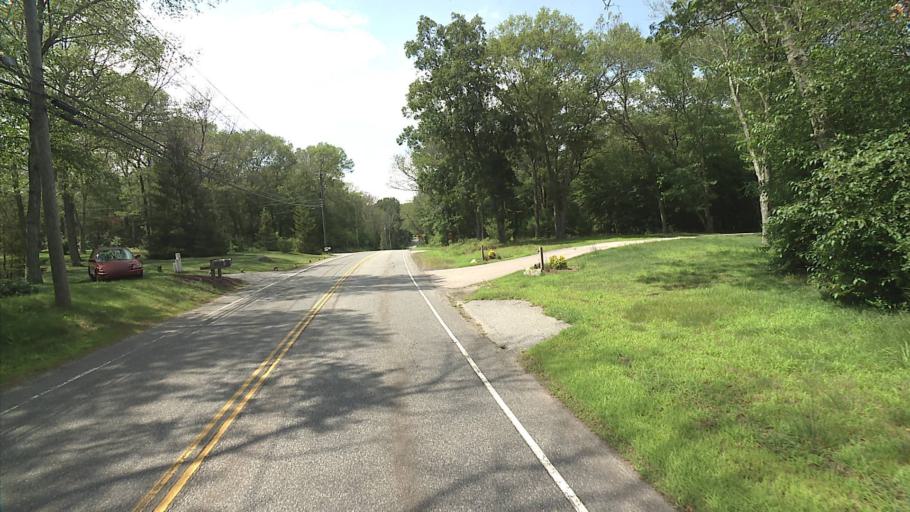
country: US
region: Connecticut
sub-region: New London County
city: Montville Center
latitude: 41.5004
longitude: -72.2311
